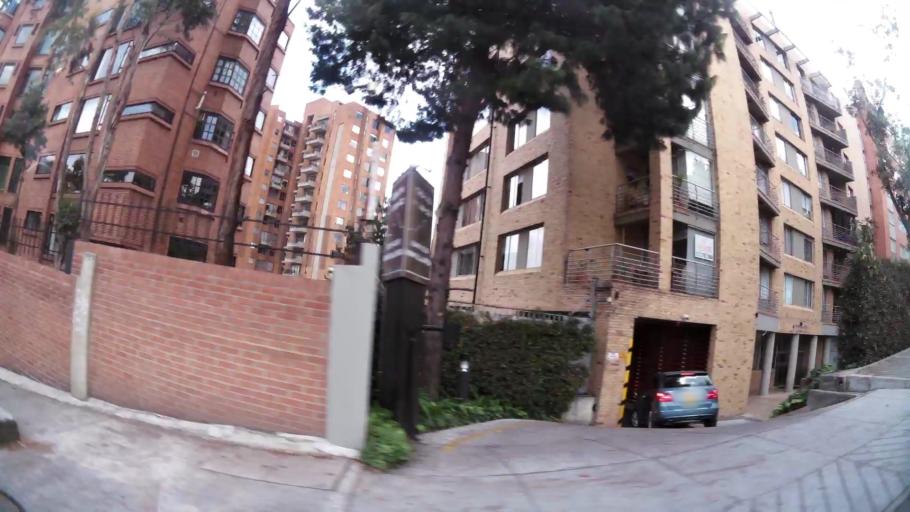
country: CO
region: Cundinamarca
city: Cota
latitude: 4.7327
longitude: -74.0747
